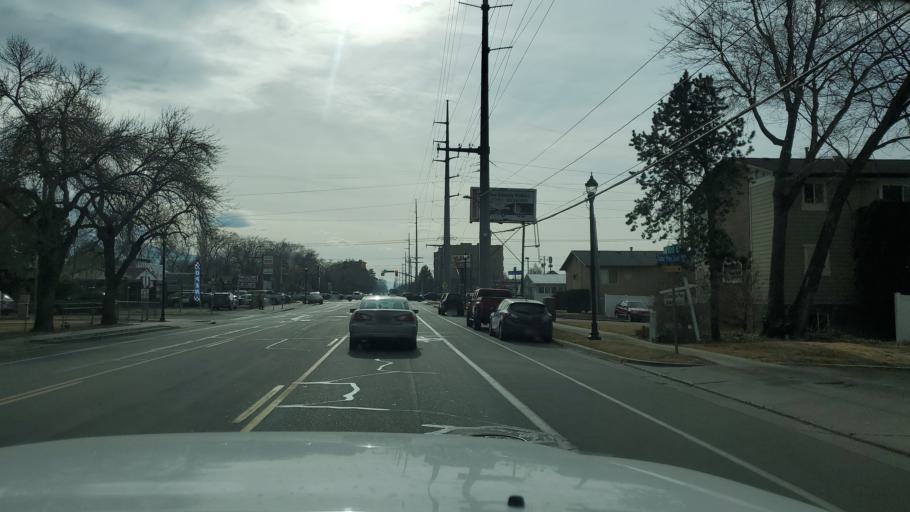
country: US
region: Utah
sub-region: Salt Lake County
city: Millcreek
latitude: 40.6883
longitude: -111.8656
